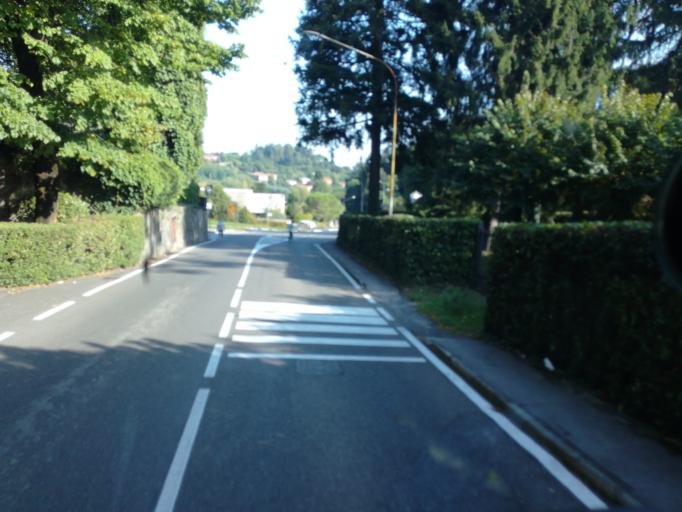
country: IT
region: Lombardy
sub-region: Provincia di Lecco
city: Monticello
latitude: 45.7169
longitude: 9.3204
